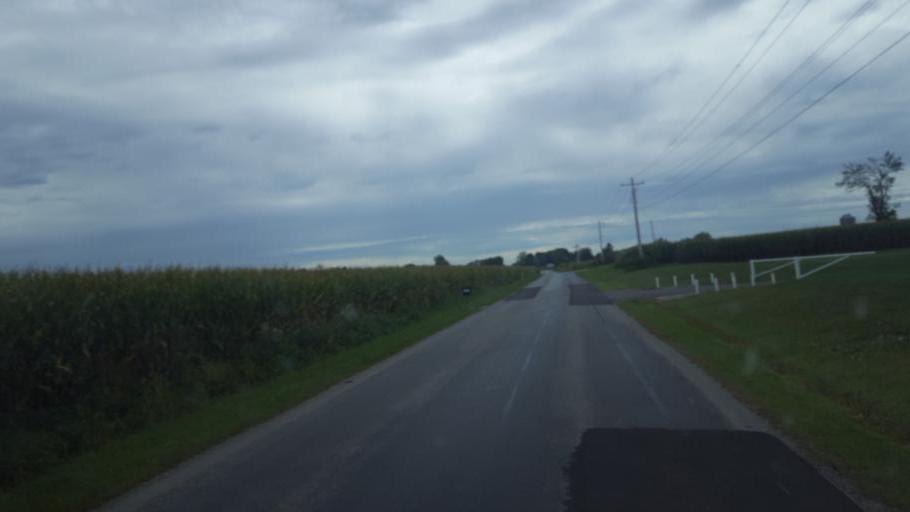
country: US
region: Ohio
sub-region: Knox County
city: Centerburg
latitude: 40.2988
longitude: -82.7251
